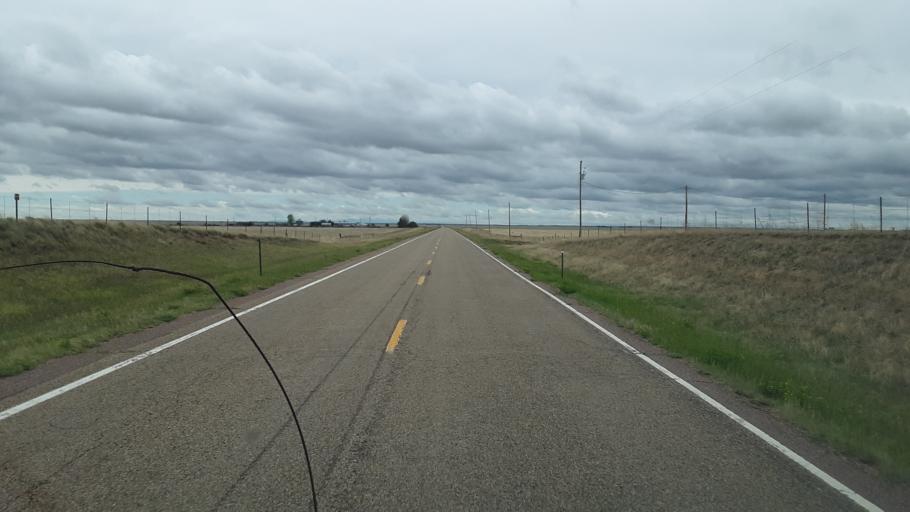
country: US
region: Colorado
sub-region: Lincoln County
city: Limon
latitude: 38.8387
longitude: -103.8818
